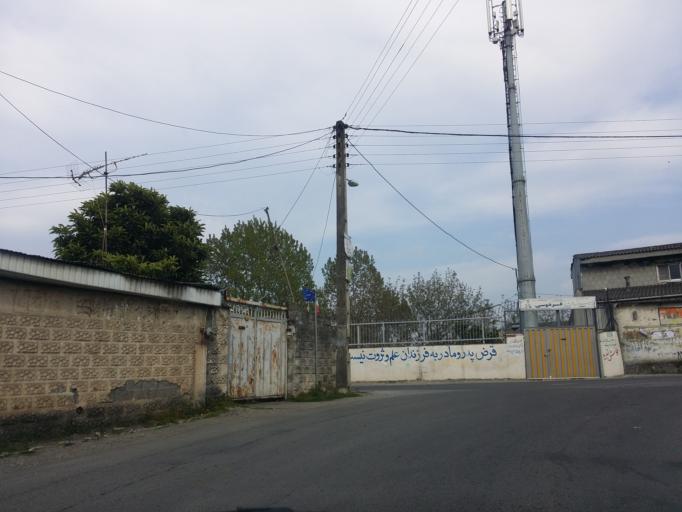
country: IR
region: Mazandaran
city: Chalus
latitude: 36.6514
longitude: 51.4113
